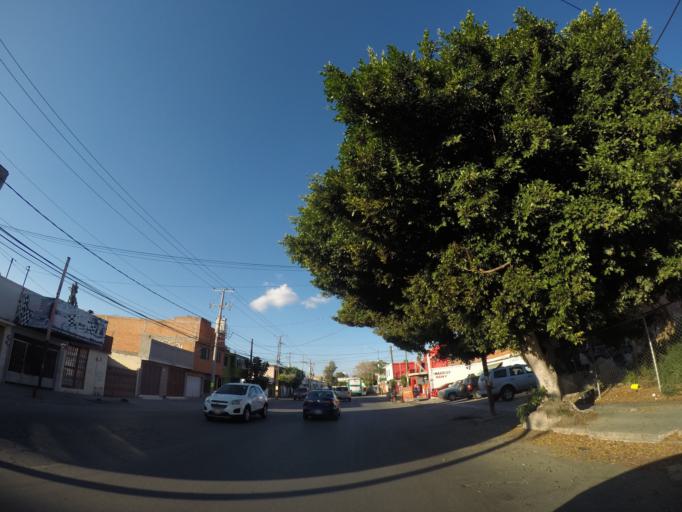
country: MX
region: San Luis Potosi
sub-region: San Luis Potosi
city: San Luis Potosi
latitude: 22.1780
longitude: -100.9961
